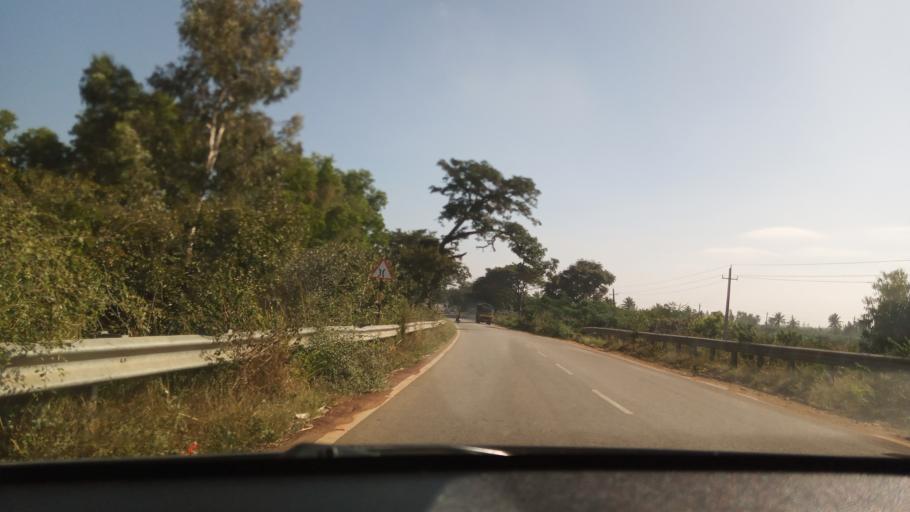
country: IN
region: Karnataka
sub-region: Bangalore Rural
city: Vijayapura
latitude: 13.2795
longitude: 77.7617
